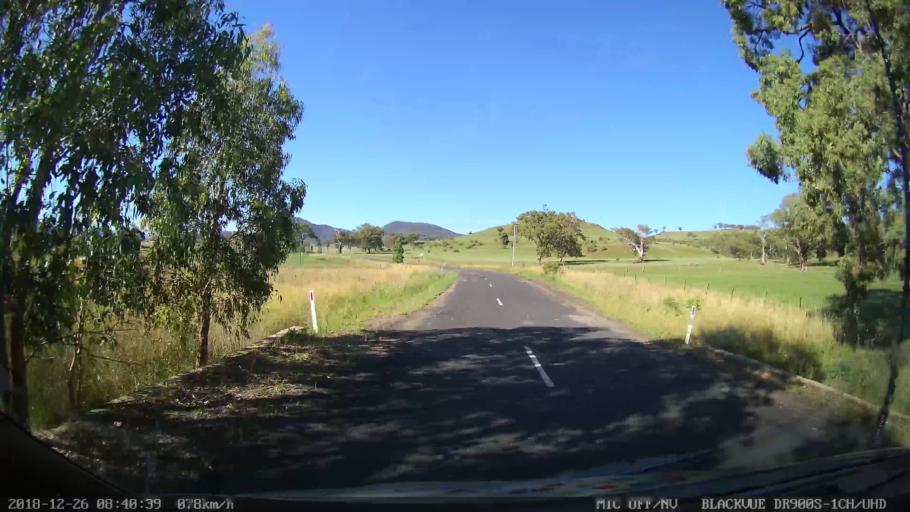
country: AU
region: New South Wales
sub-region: Mid-Western Regional
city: Kandos
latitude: -32.4692
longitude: 150.0749
